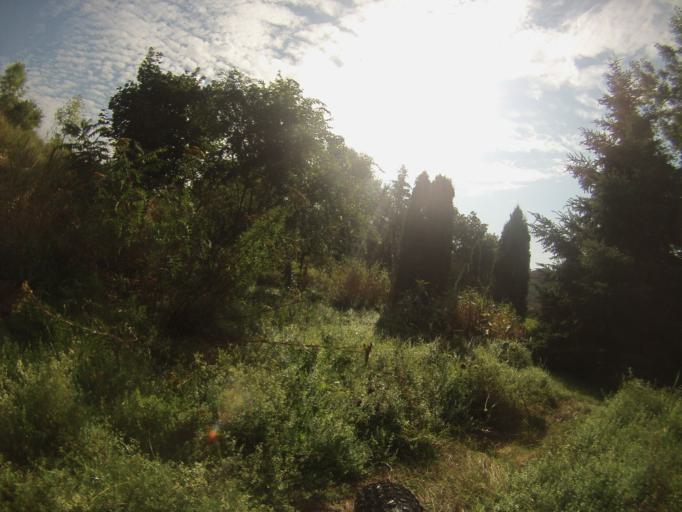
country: CA
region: Ontario
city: Ottawa
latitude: 45.3779
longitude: -75.6044
